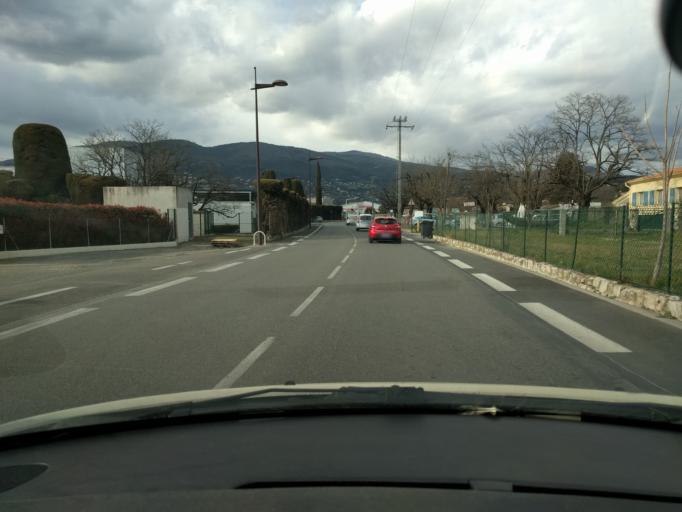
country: FR
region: Provence-Alpes-Cote d'Azur
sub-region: Departement des Alpes-Maritimes
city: Mouans-Sartoux
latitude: 43.6377
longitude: 6.9565
